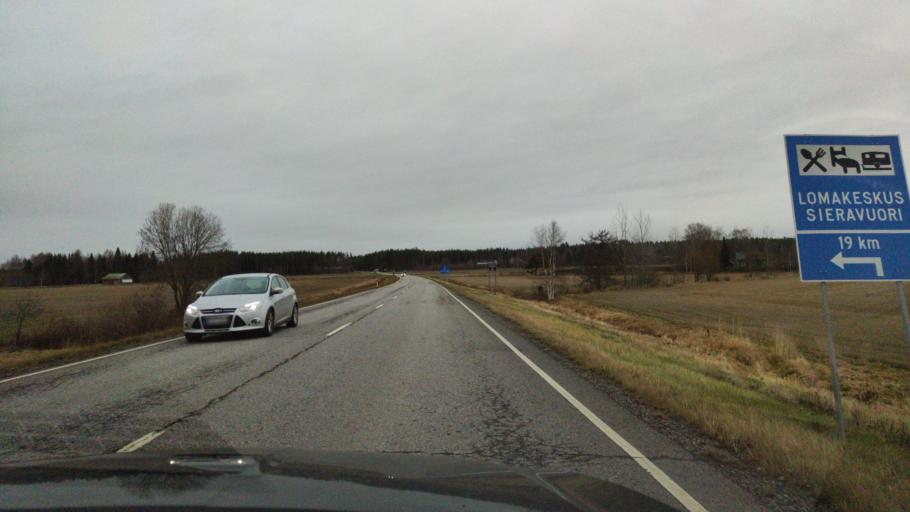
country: FI
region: Varsinais-Suomi
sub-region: Loimaa
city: Ylaene
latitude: 60.8826
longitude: 22.3986
